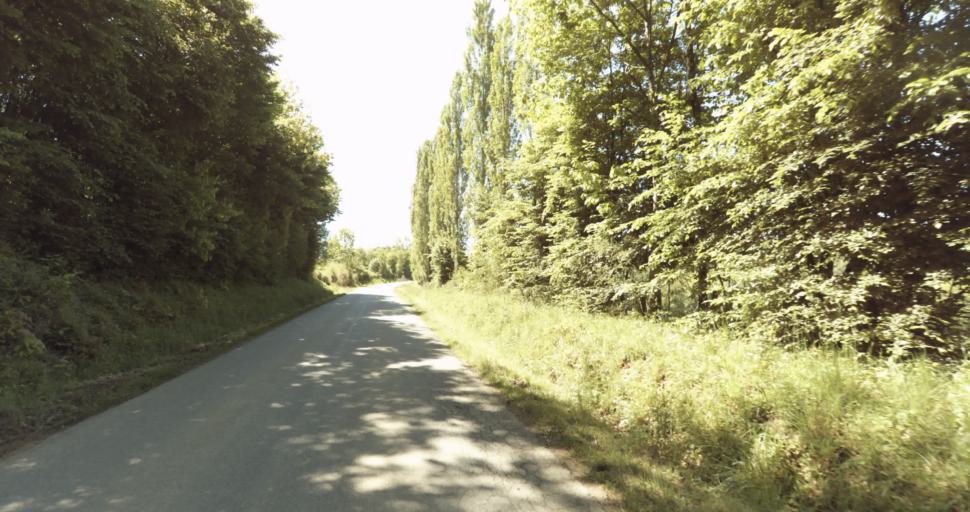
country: FR
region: Limousin
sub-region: Departement de la Haute-Vienne
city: Le Vigen
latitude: 45.7451
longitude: 1.3081
